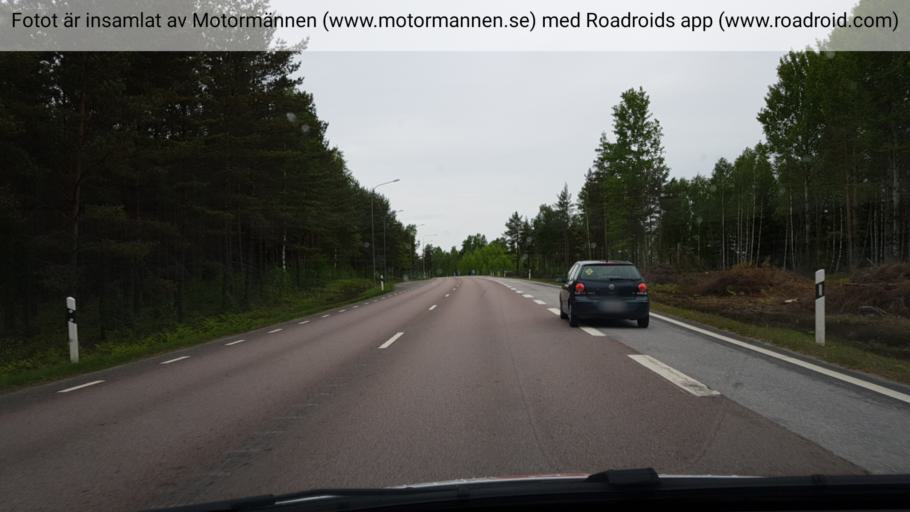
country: SE
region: Kalmar
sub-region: Hultsfreds Kommun
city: Hultsfred
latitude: 57.4704
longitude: 15.8404
